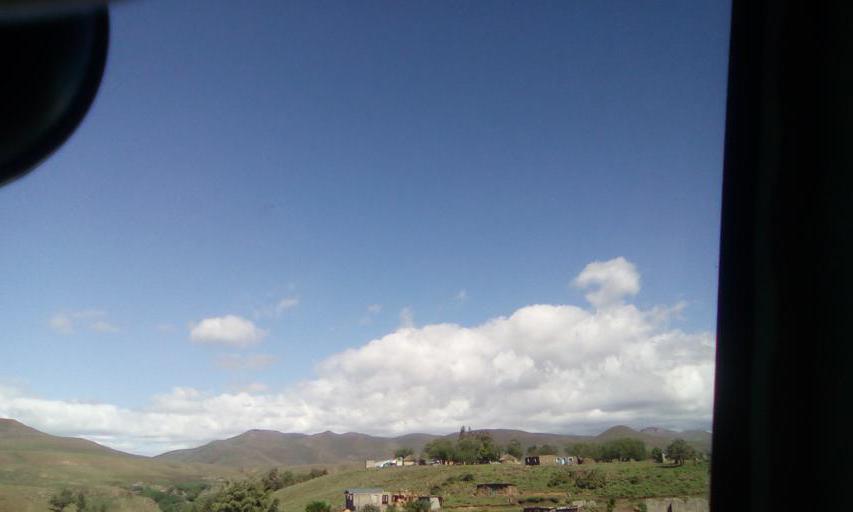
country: LS
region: Maseru
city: Nako
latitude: -29.8452
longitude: 28.0571
